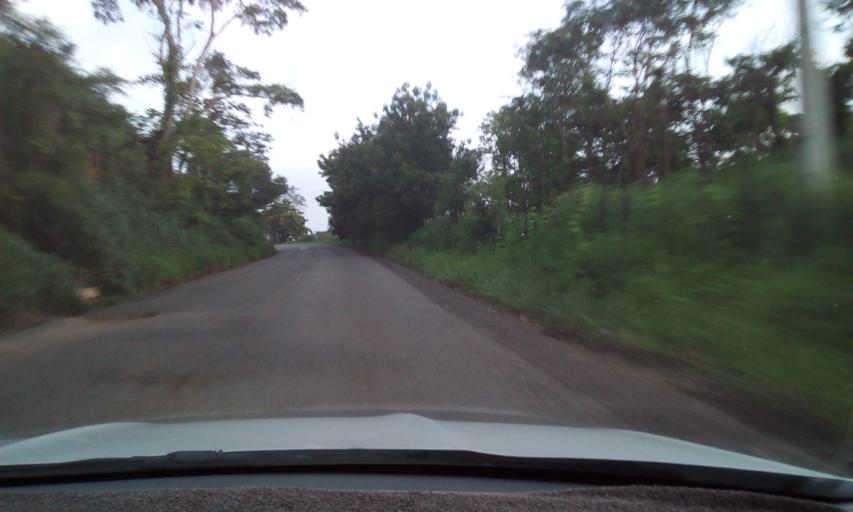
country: BR
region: Pernambuco
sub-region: Condado
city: Condado
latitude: -7.6016
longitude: -35.2126
